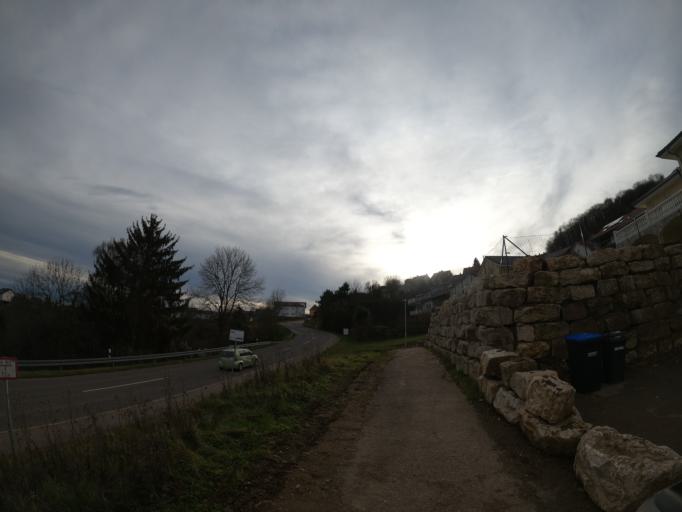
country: DE
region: Baden-Wuerttemberg
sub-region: Regierungsbezirk Stuttgart
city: Ottenbach
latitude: 48.7442
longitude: 9.7221
